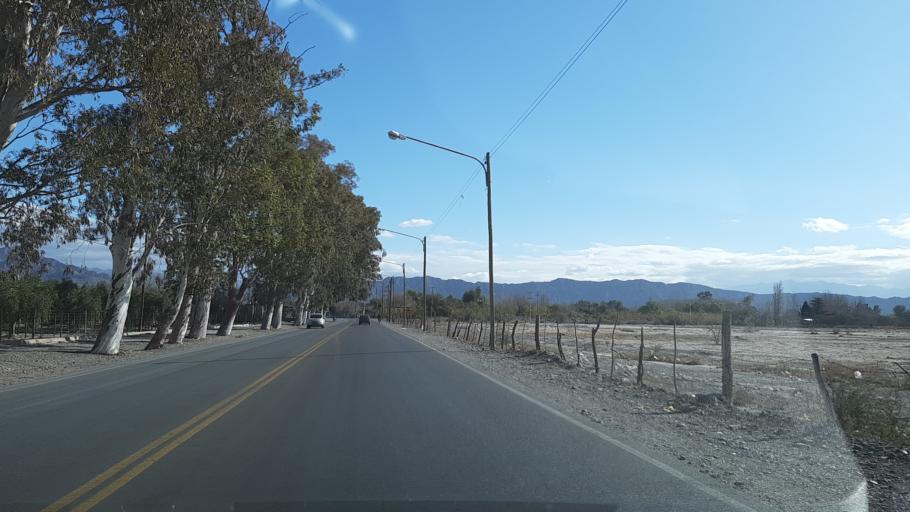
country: AR
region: San Juan
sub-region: Departamento de Rivadavia
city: Rivadavia
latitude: -31.5390
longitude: -68.6094
